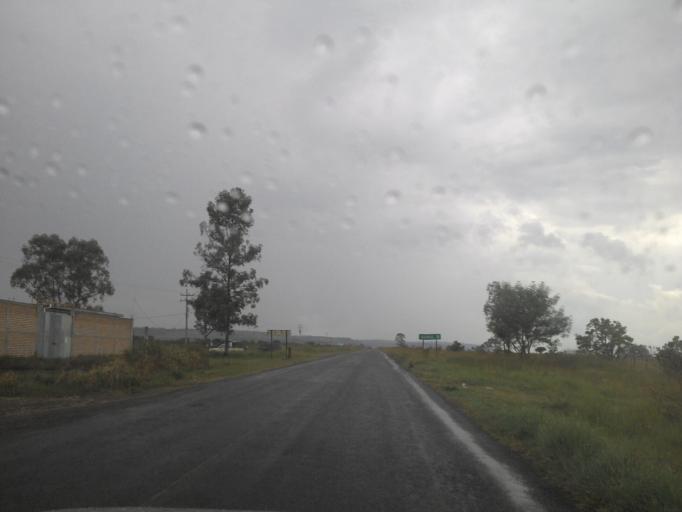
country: MX
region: Jalisco
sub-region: Arandas
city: Santiaguito (Santiaguito de Velazquez)
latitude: 20.8098
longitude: -102.2167
